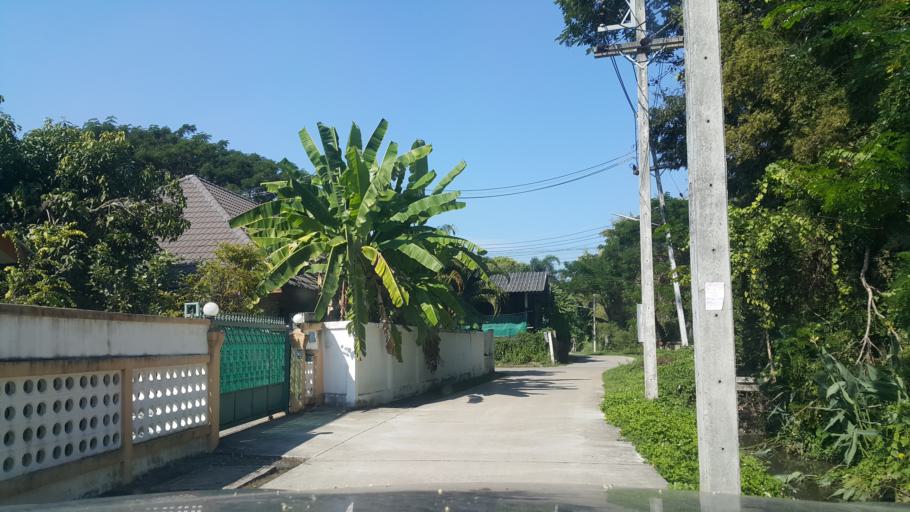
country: TH
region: Chiang Mai
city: Chiang Mai
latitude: 18.7748
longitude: 99.0369
